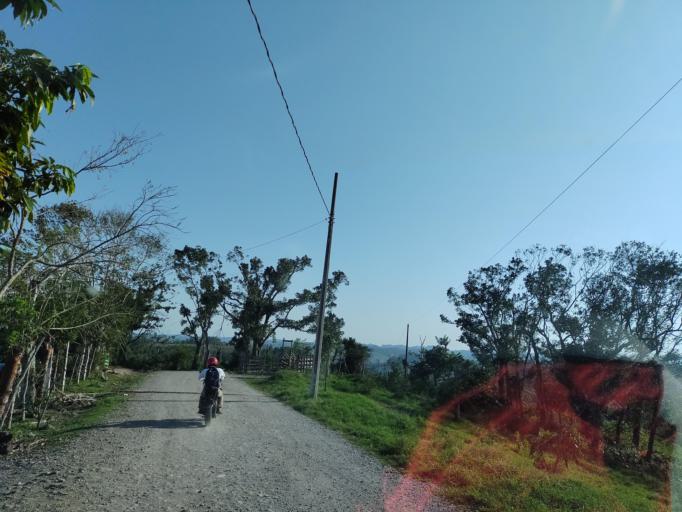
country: MX
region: Veracruz
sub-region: Papantla
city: Polutla
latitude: 20.4552
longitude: -97.2412
